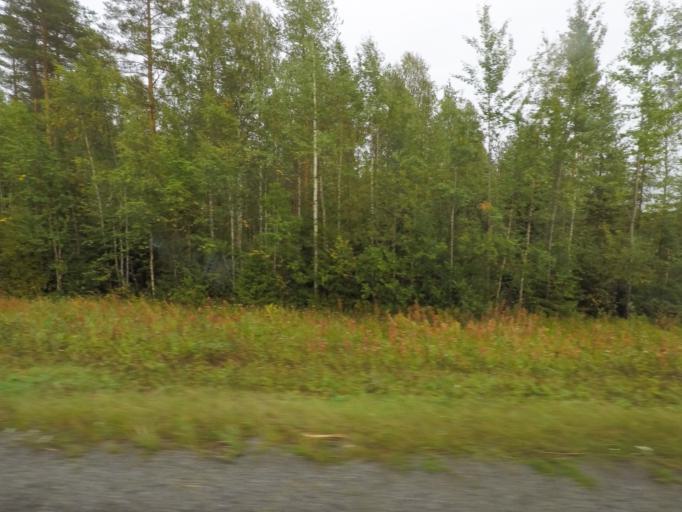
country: FI
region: Southern Savonia
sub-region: Pieksaemaeki
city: Joroinen
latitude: 62.0442
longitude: 27.8017
